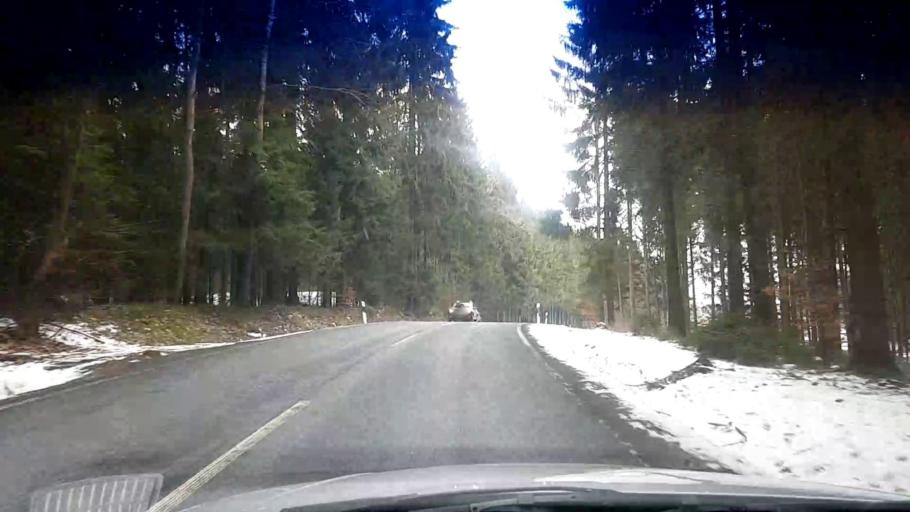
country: DE
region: Bavaria
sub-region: Upper Franconia
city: Steinbach
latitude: 50.1812
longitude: 11.6690
